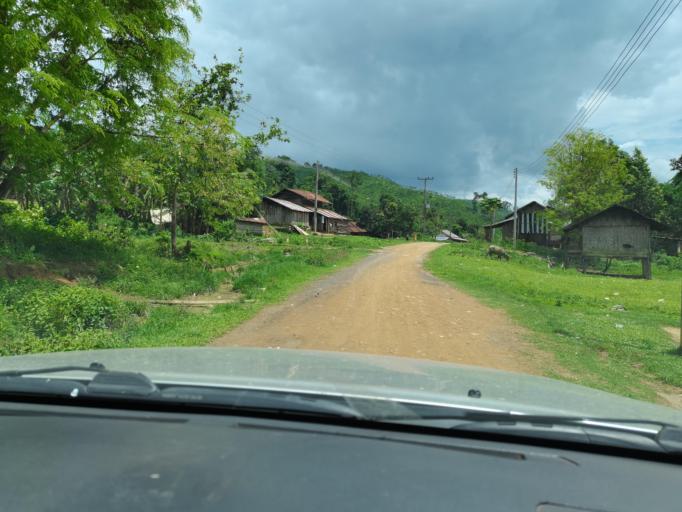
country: LA
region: Loungnamtha
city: Muang Long
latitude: 20.7244
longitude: 101.0143
